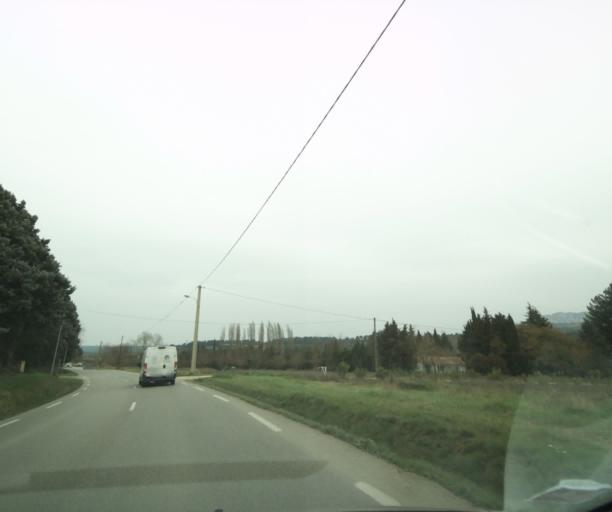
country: FR
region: Provence-Alpes-Cote d'Azur
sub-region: Departement des Bouches-du-Rhone
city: Fuveau
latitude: 43.4737
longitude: 5.5433
